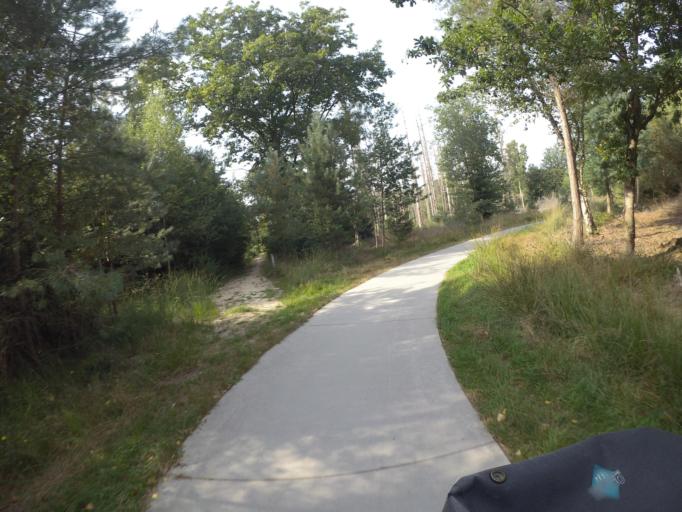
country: NL
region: Drenthe
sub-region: Gemeente Westerveld
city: Dwingeloo
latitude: 52.9044
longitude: 6.3623
